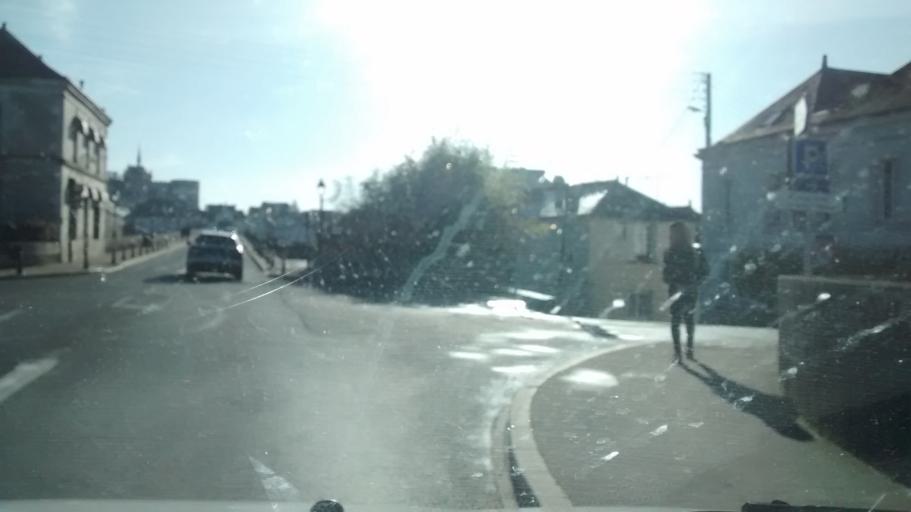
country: FR
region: Centre
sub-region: Departement d'Indre-et-Loire
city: Amboise
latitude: 47.4161
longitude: 0.9825
